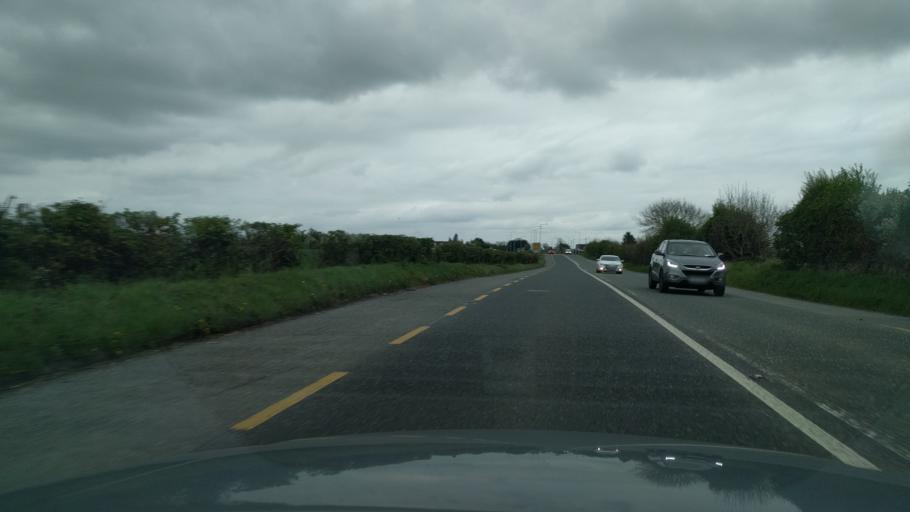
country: IE
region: Leinster
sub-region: Fingal County
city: Blanchardstown
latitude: 53.4481
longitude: -6.3433
